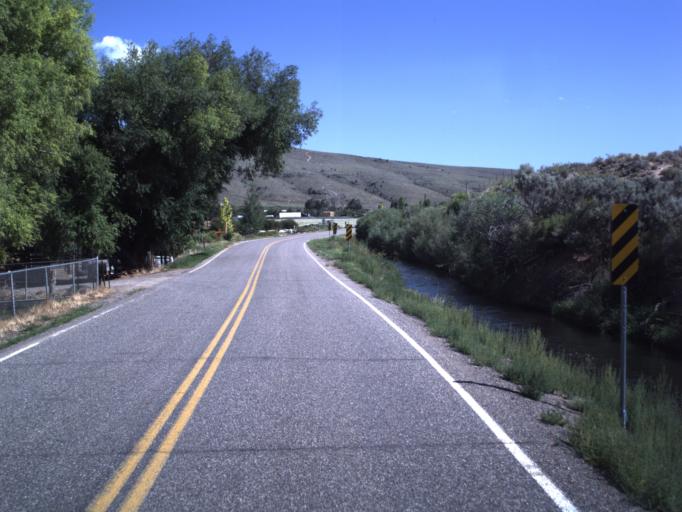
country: US
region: Utah
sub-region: Wayne County
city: Loa
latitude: 38.4632
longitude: -111.5955
